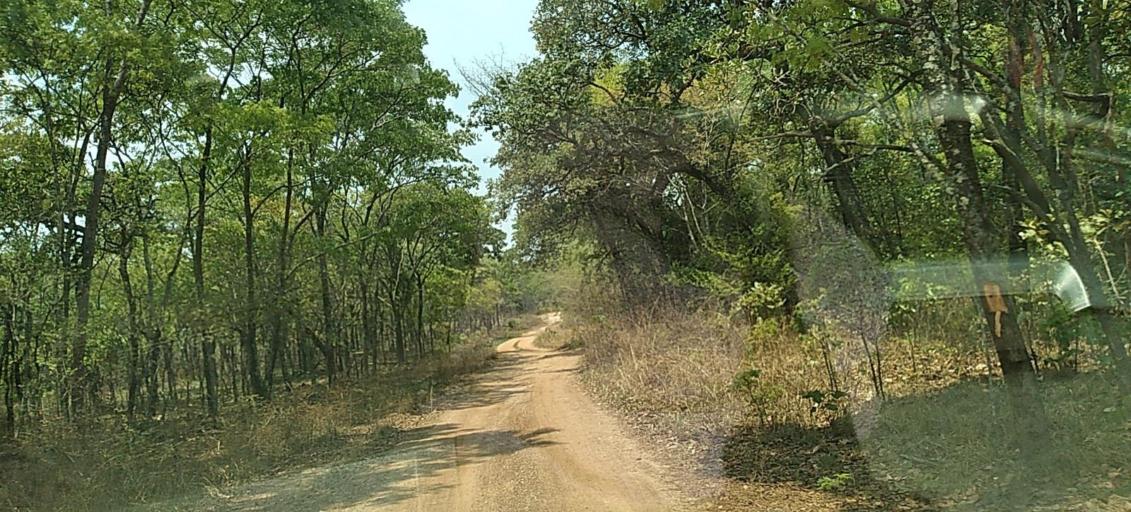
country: ZM
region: Copperbelt
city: Chingola
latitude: -12.7850
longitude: 27.6644
